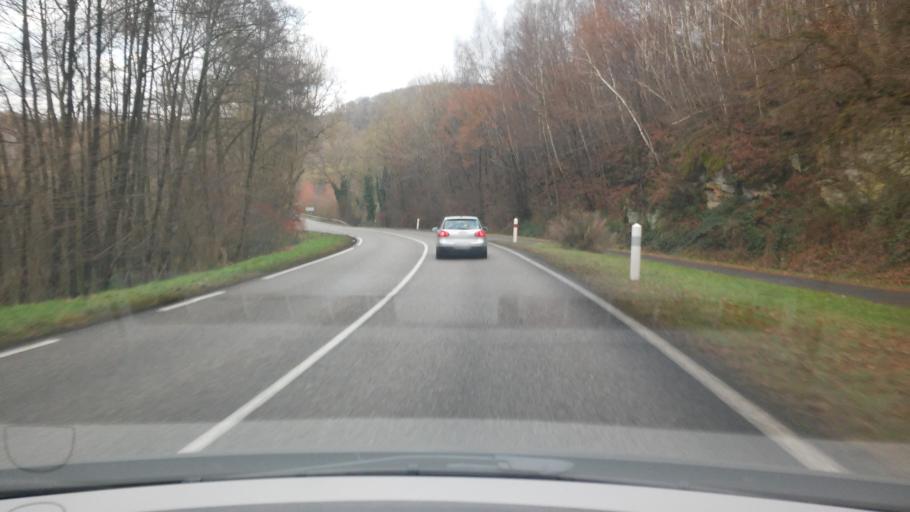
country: FR
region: Lorraine
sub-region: Departement de la Moselle
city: Hombourg-Haut
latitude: 49.1132
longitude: 6.7599
